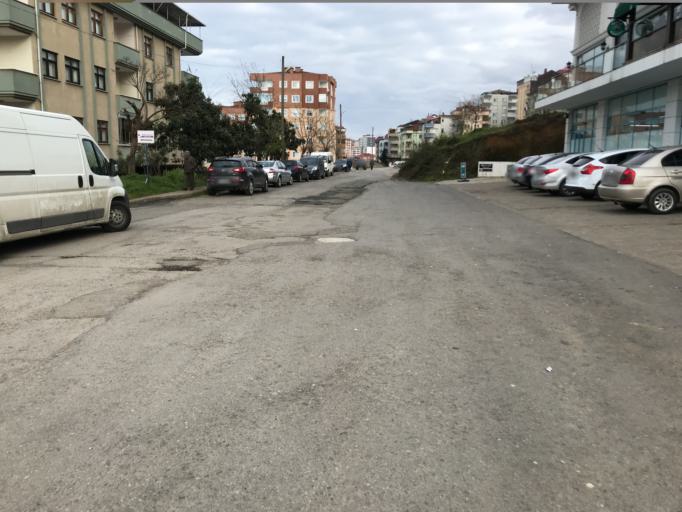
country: TR
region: Trabzon
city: Trabzon
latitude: 40.9902
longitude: 39.7787
